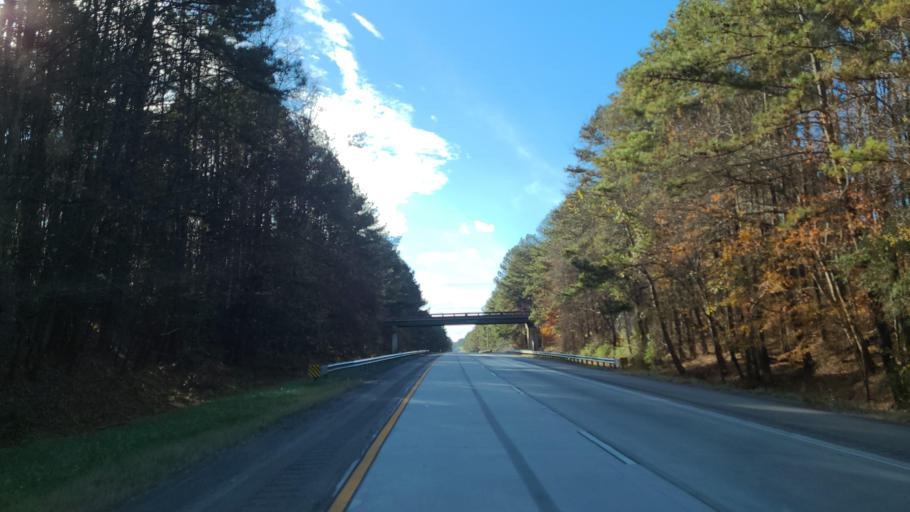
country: US
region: Georgia
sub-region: Carroll County
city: Temple
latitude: 33.6995
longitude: -85.0677
